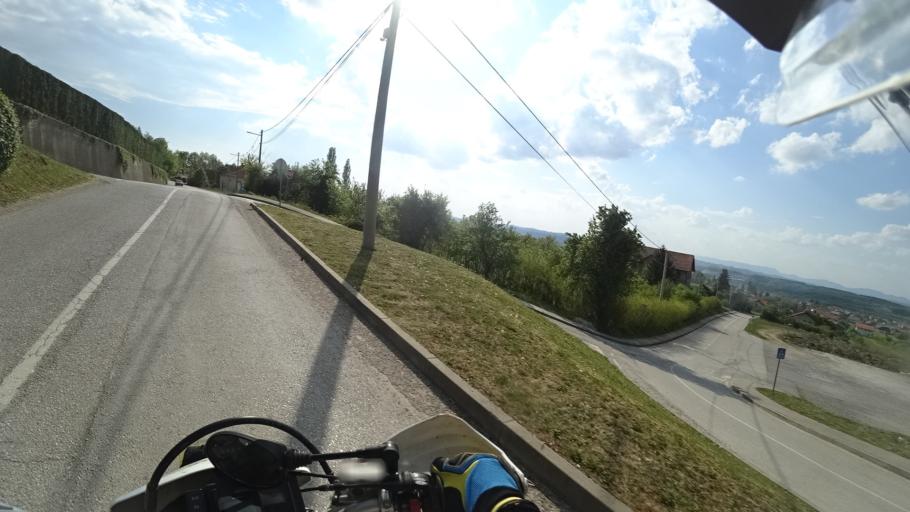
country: HR
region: Zagrebacka
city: Jablanovec
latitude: 45.8969
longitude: 15.8802
